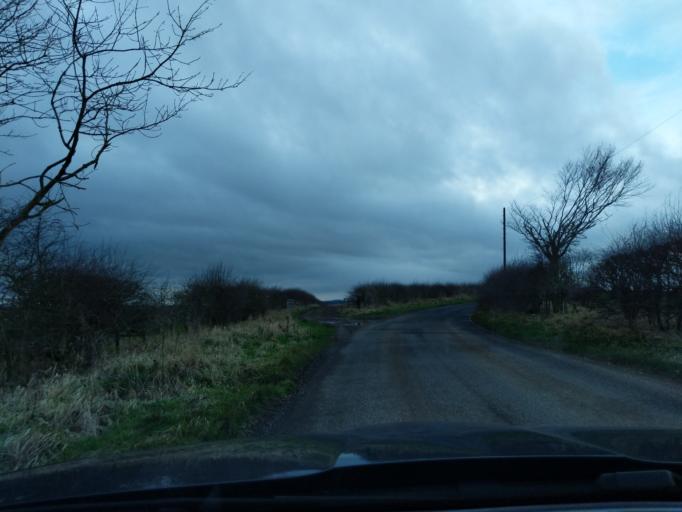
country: GB
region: England
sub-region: Northumberland
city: Ford
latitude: 55.7122
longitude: -2.1133
